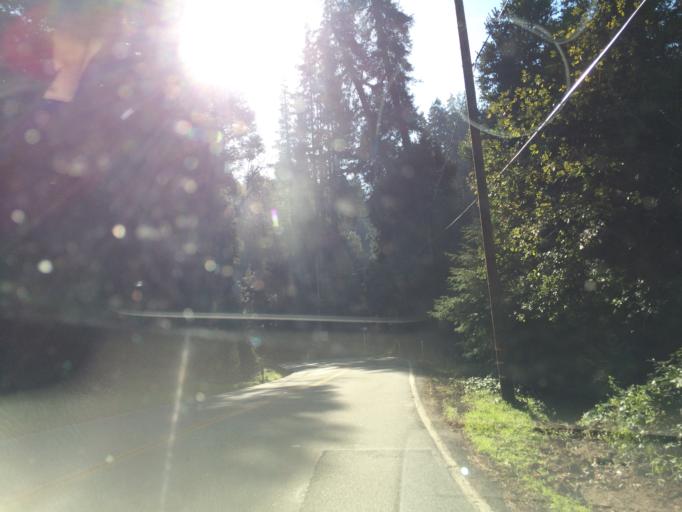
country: US
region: California
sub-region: Santa Cruz County
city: Boulder Creek
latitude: 37.1388
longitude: -122.1477
